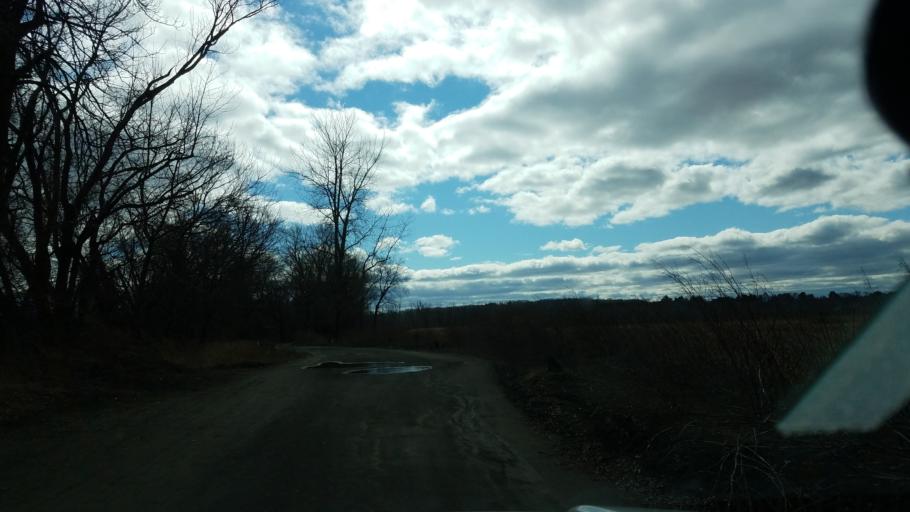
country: US
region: Connecticut
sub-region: Hartford County
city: Wethersfield
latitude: 41.6934
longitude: -72.6383
